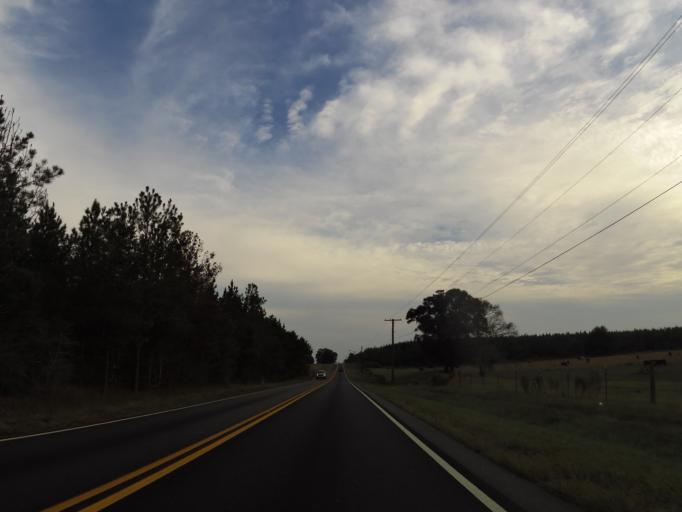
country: US
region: Alabama
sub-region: Escambia County
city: Atmore
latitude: 31.1892
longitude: -87.4638
